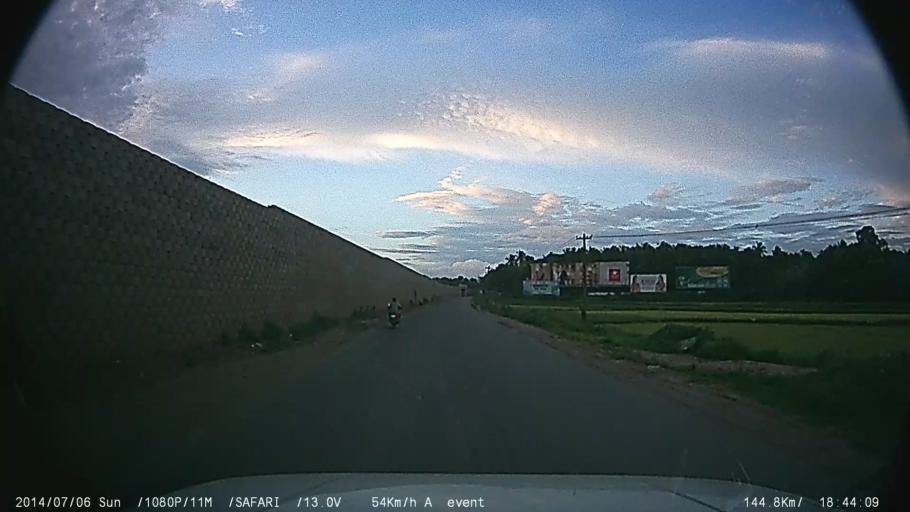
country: IN
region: Kerala
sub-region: Palakkad district
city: Palakkad
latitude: 10.6628
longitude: 76.5724
